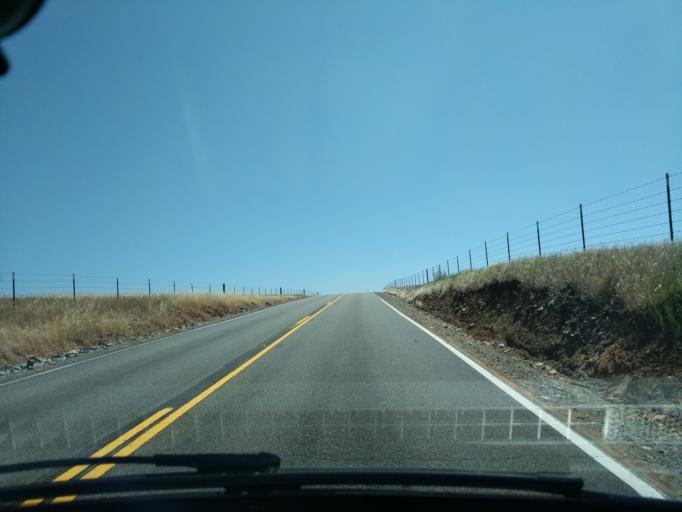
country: US
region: California
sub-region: Stanislaus County
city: East Oakdale
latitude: 37.9373
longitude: -120.7934
